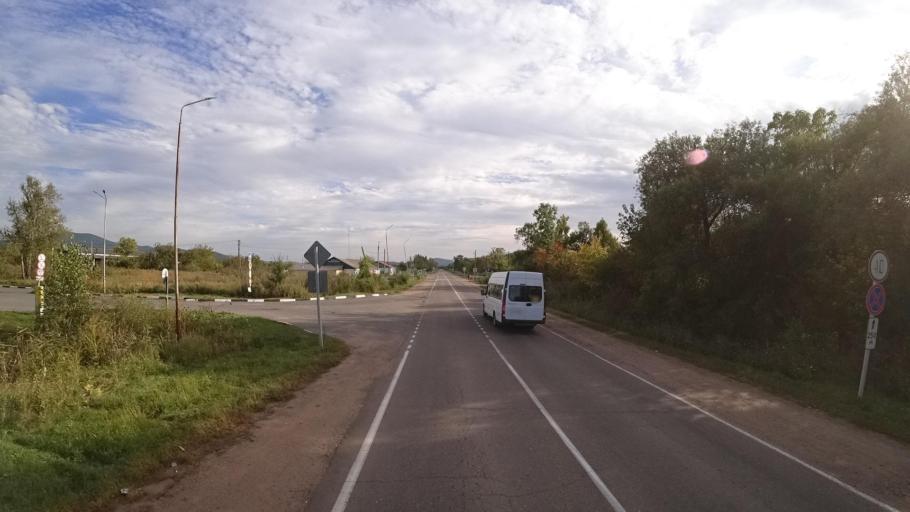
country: RU
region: Primorskiy
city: Dostoyevka
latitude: 44.2945
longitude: 133.4265
